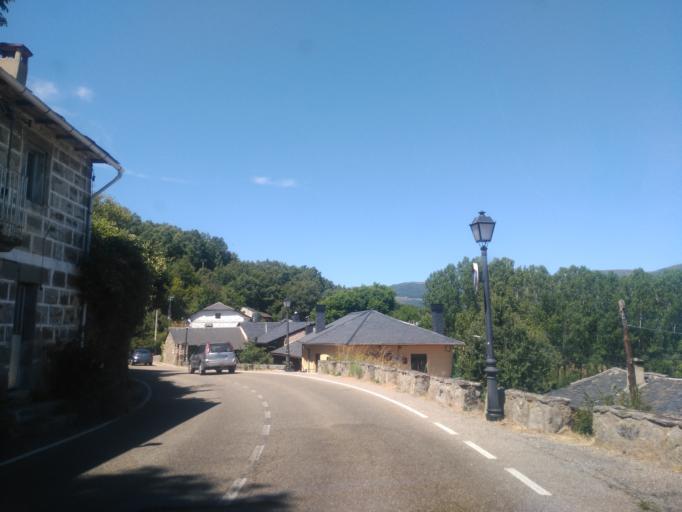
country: ES
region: Castille and Leon
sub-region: Provincia de Zamora
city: Galende
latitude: 42.1046
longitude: -6.6633
